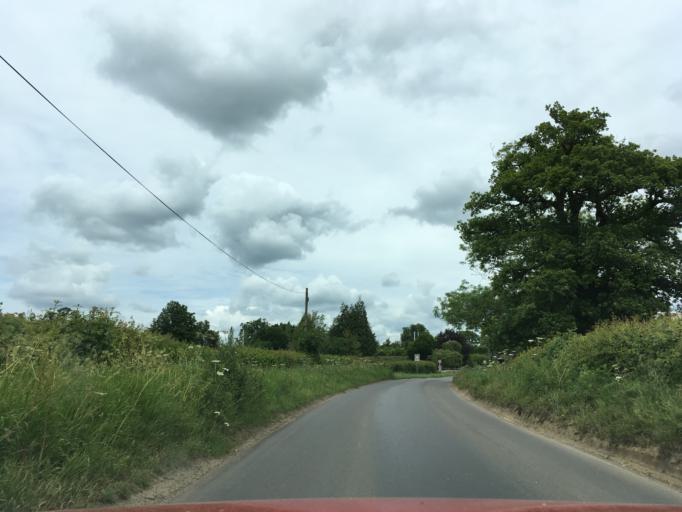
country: GB
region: England
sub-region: Wiltshire
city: Charlton
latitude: 51.5543
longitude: -2.0511
